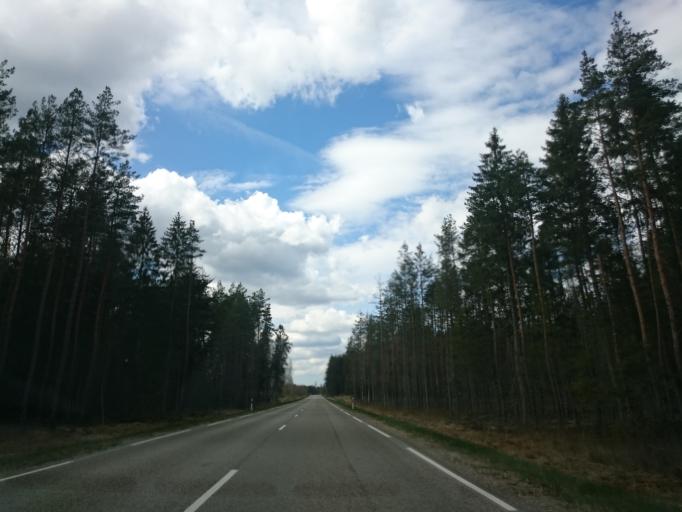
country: LV
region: Kuldigas Rajons
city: Kuldiga
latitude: 56.9514
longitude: 22.2545
